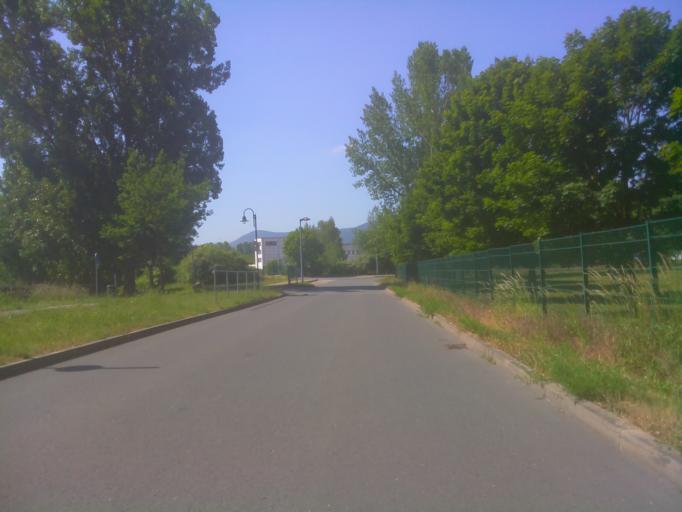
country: DE
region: Thuringia
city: Rudolstadt
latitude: 50.6911
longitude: 11.3359
